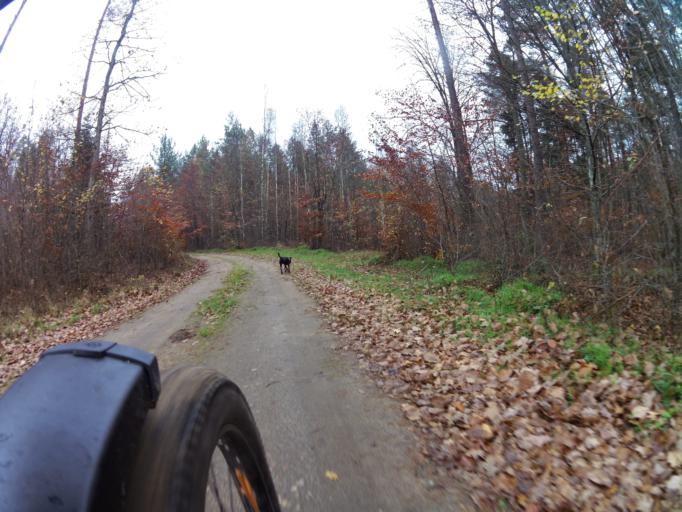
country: PL
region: Pomeranian Voivodeship
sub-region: Powiat wejherowski
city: Orle
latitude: 54.6974
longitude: 18.1566
